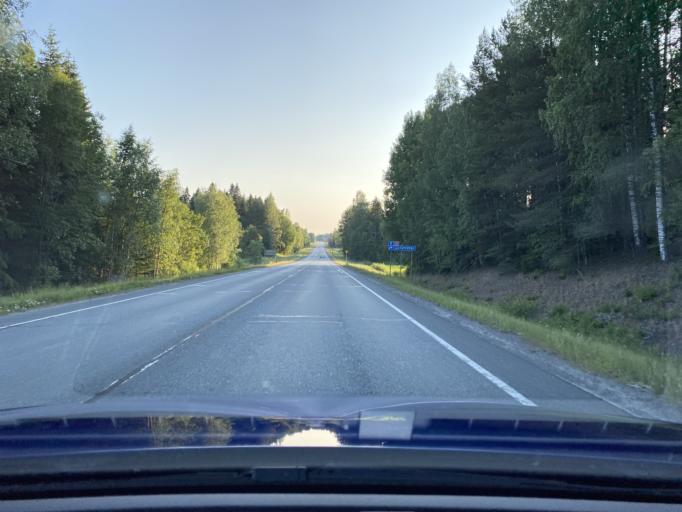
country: FI
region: Haeme
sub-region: Forssa
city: Tammela
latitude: 60.8296
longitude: 23.8488
